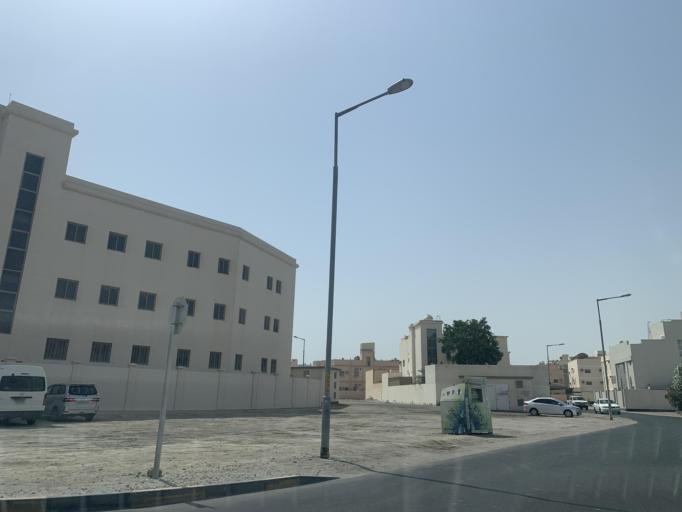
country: BH
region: Northern
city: Madinat `Isa
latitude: 26.1890
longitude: 50.5438
